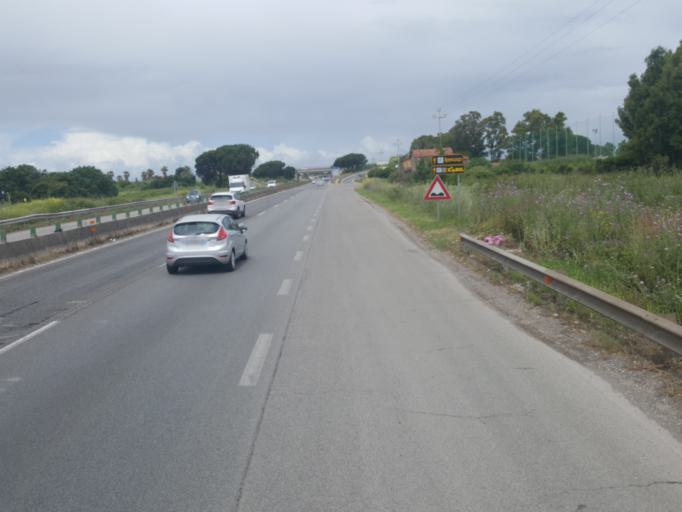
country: IT
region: Latium
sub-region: Provincia di Latina
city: Aprilia
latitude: 41.5700
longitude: 12.6676
